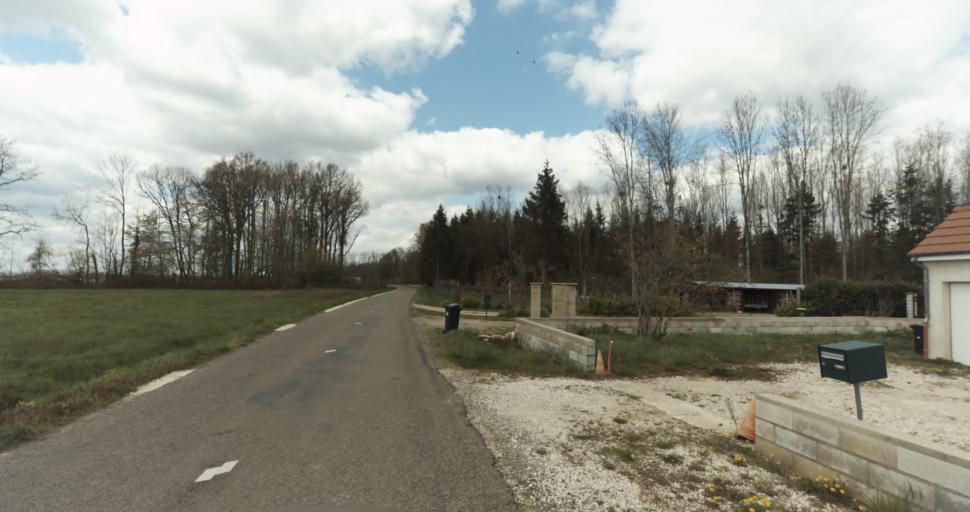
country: FR
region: Bourgogne
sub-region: Departement de la Cote-d'Or
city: Auxonne
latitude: 47.1805
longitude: 5.4185
